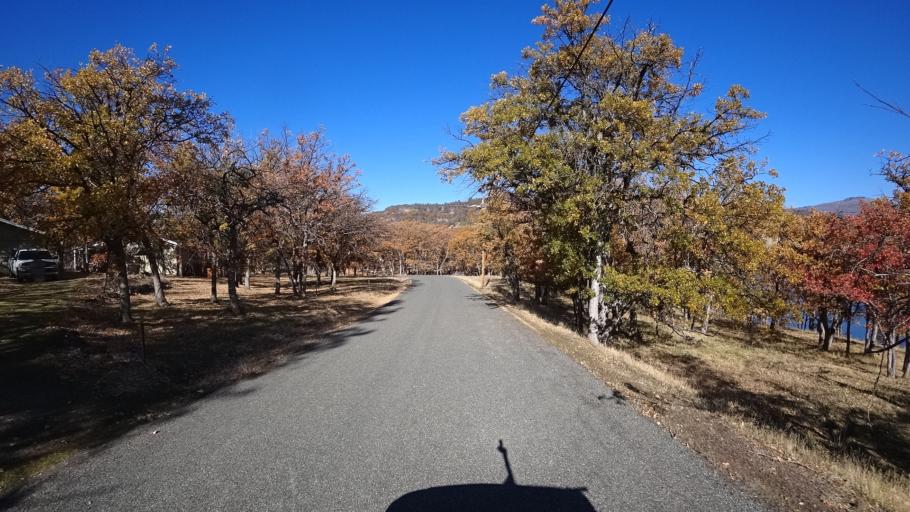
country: US
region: California
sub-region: Siskiyou County
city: Montague
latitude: 41.9781
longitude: -122.3242
